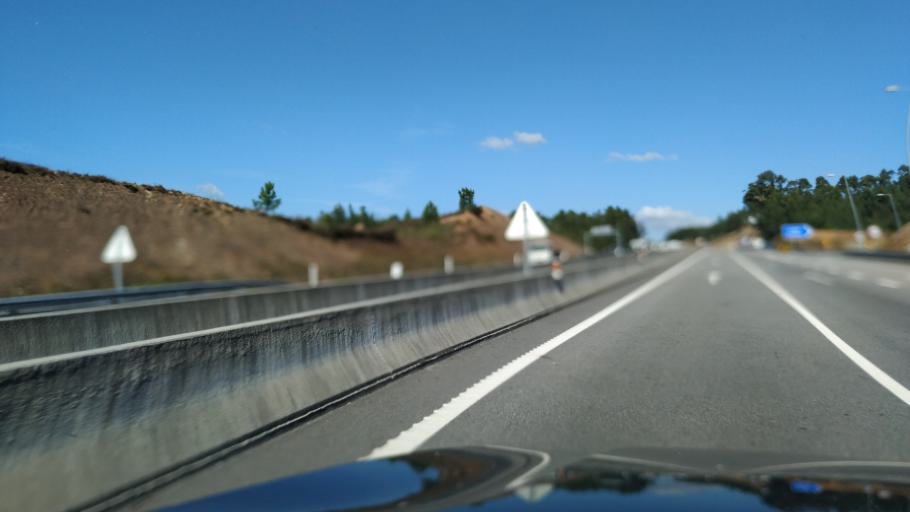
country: PT
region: Porto
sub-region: Vila Nova de Gaia
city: Sandim
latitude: 41.0390
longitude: -8.4940
